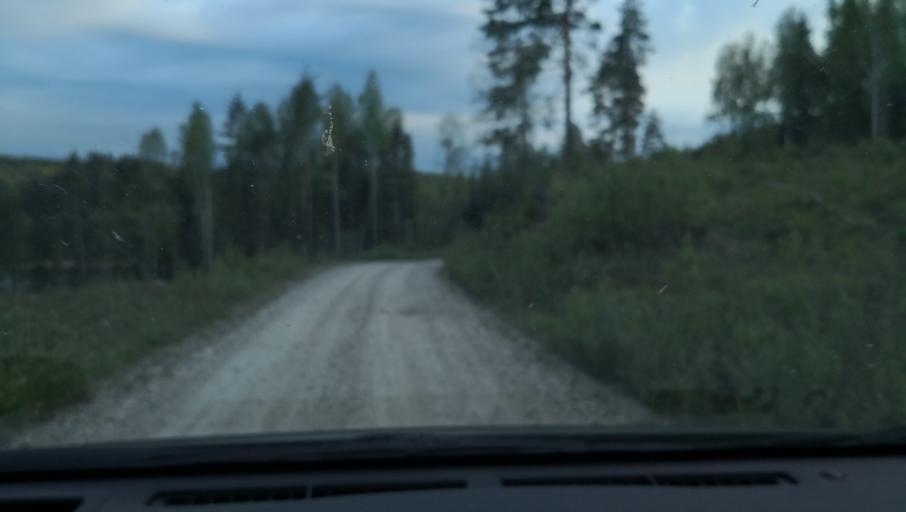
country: SE
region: Vaestmanland
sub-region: Skinnskattebergs Kommun
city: Skinnskatteberg
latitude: 59.7987
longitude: 15.4732
